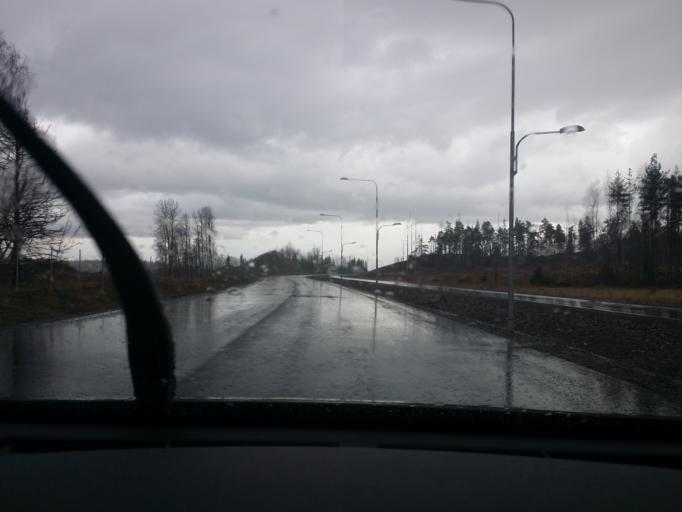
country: SE
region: Soedermanland
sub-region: Eskilstuna Kommun
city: Arla
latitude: 59.3556
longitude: 16.7011
